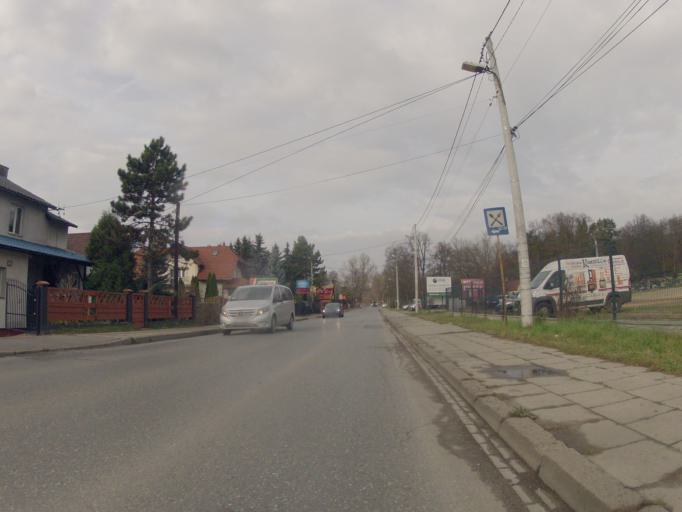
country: PL
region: Lesser Poland Voivodeship
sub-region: Powiat krakowski
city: Rzaska
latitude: 50.0862
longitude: 19.8428
